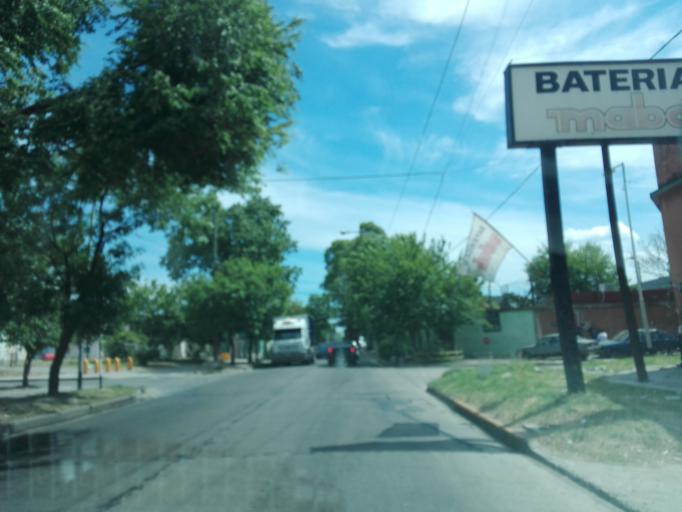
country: AR
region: Buenos Aires
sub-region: Partido de Lanus
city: Lanus
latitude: -34.6997
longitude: -58.3630
